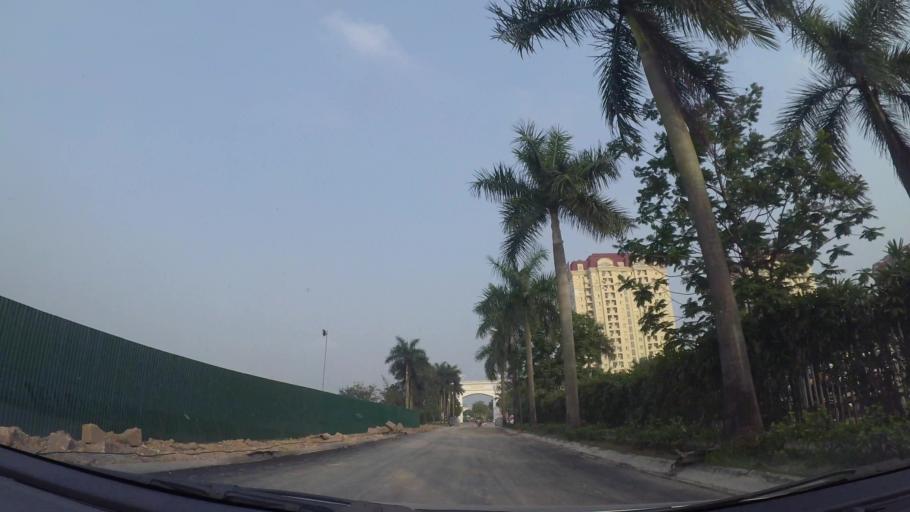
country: VN
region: Ha Noi
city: Tay Ho
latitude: 21.0758
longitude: 105.8089
